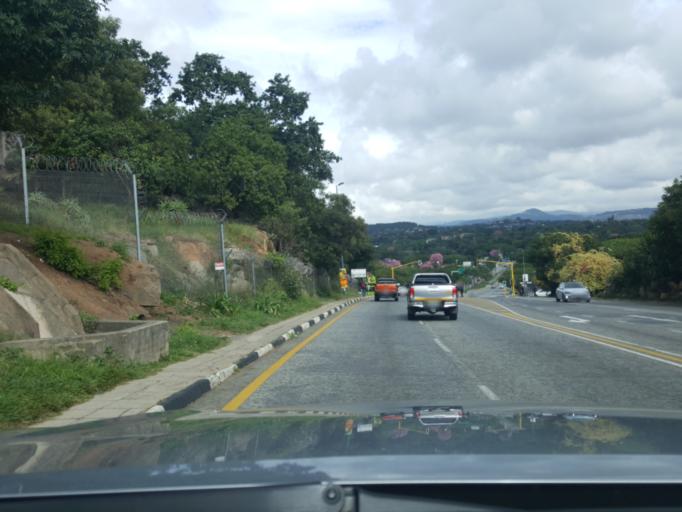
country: ZA
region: Mpumalanga
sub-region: Ehlanzeni District
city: Nelspruit
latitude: -25.4734
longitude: 30.9761
